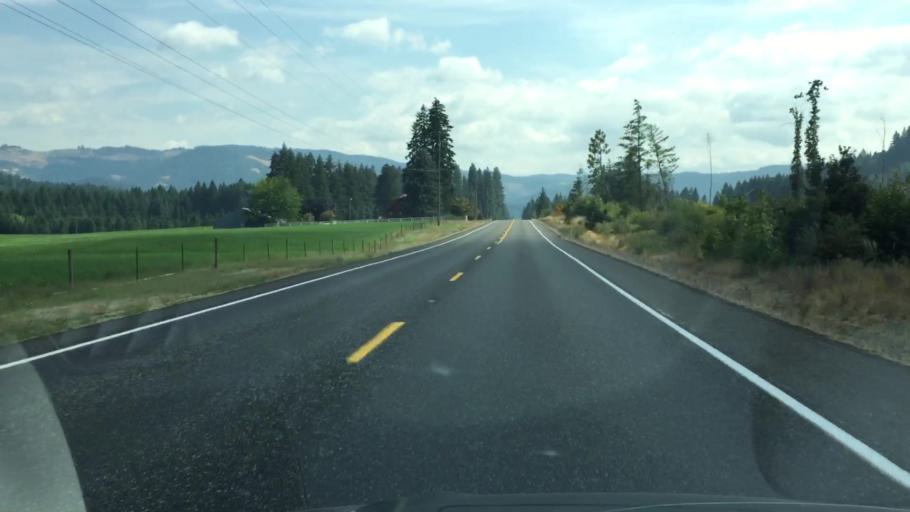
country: US
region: Washington
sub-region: Klickitat County
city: White Salmon
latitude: 45.8438
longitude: -121.5047
